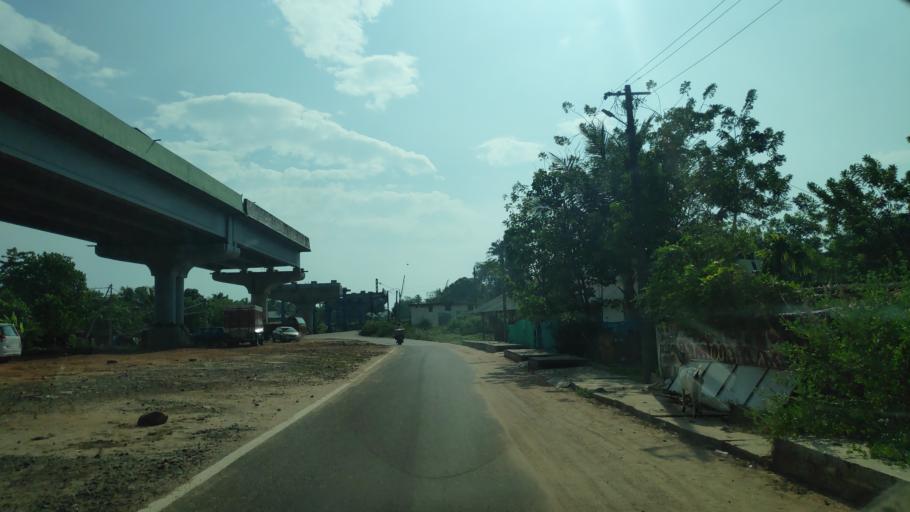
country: IN
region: Kerala
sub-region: Alappuzha
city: Alleppey
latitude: 9.5010
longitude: 76.3191
